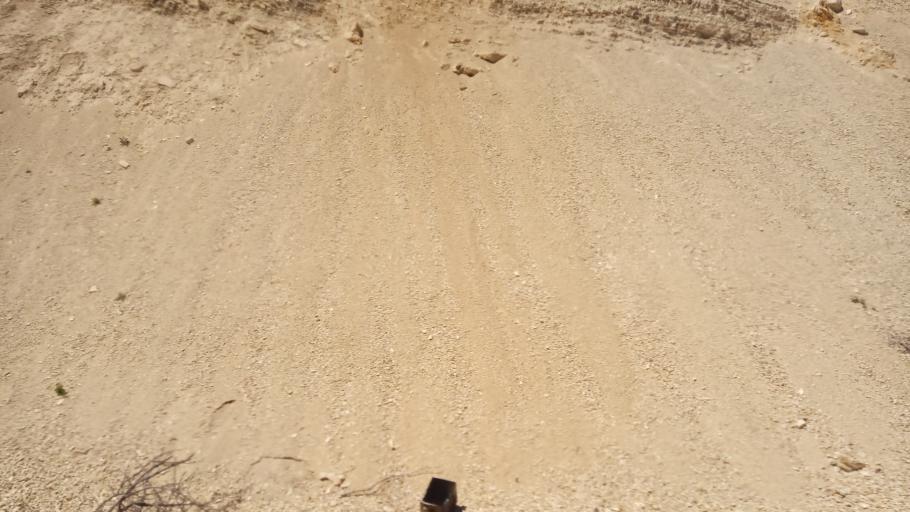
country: TR
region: Malatya
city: Darende
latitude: 38.6365
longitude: 37.4501
